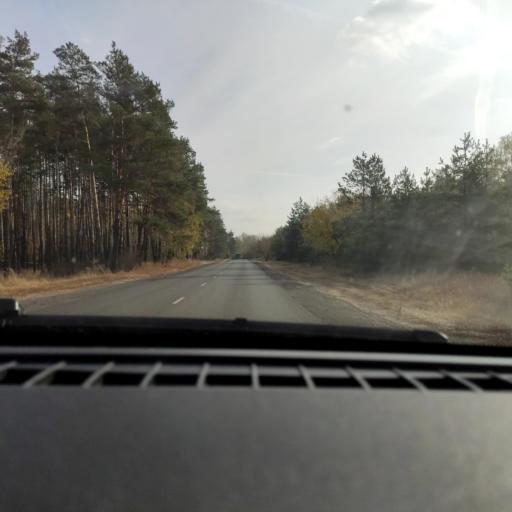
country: RU
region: Voronezj
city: Maslovka
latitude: 51.5787
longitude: 39.2909
